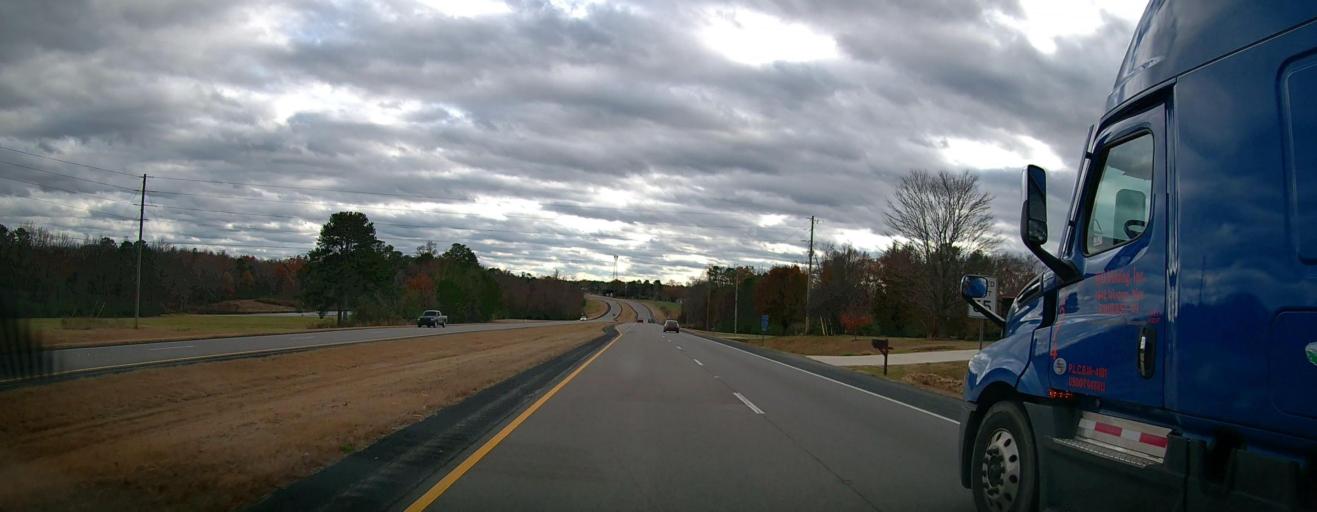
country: US
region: Alabama
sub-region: Morgan County
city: Falkville
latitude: 34.2997
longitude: -86.9974
